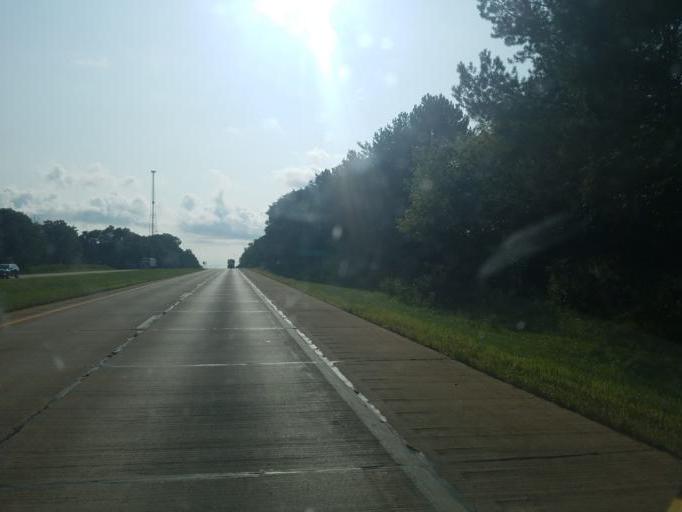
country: US
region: Ohio
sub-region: Ashland County
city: Ashland
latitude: 40.7871
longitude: -82.3425
